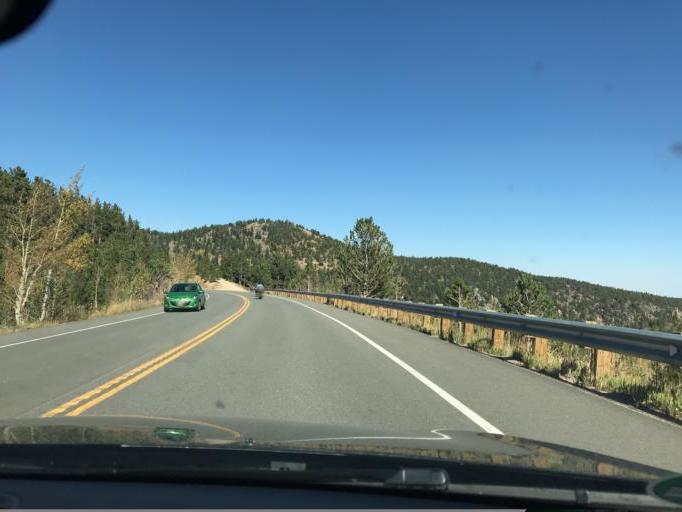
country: US
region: Colorado
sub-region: Boulder County
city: Nederland
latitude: 40.0620
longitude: -105.5177
